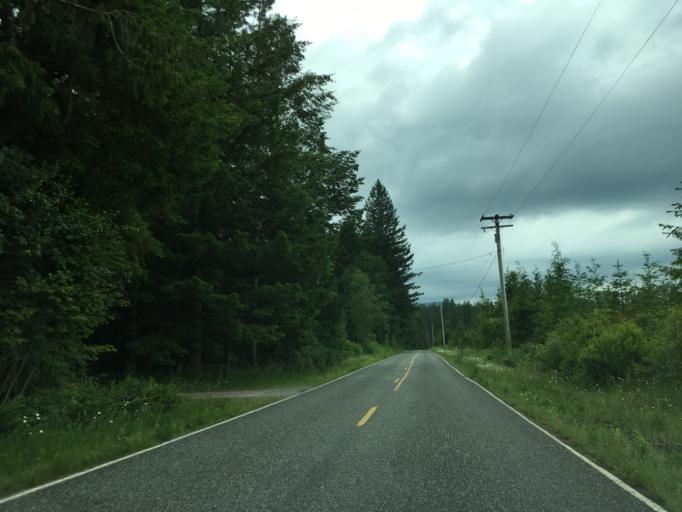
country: US
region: Washington
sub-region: Whatcom County
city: Peaceful Valley
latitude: 48.9826
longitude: -122.1152
